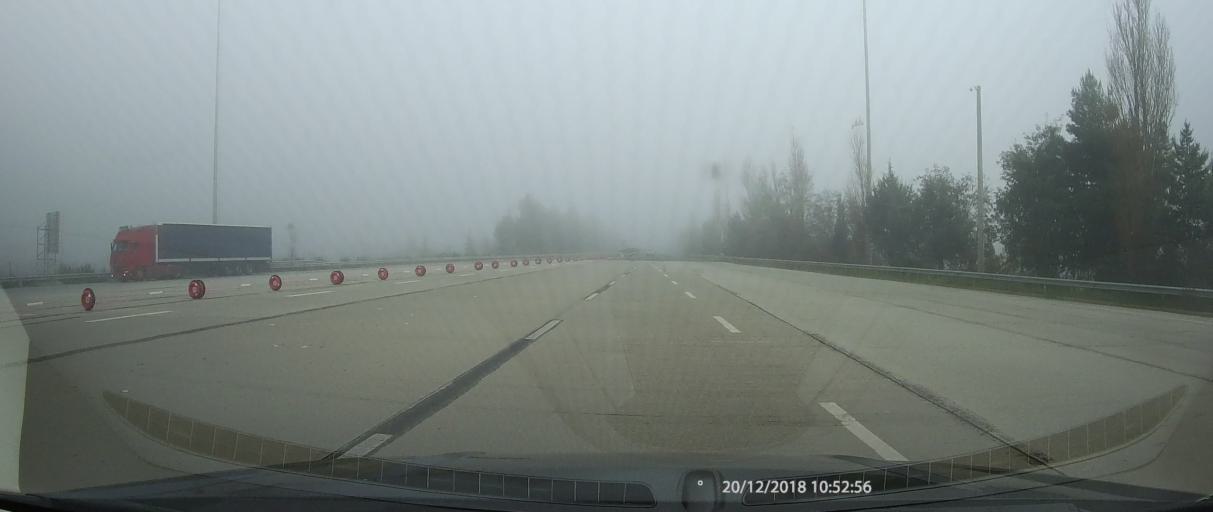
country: GR
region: Peloponnese
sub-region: Nomos Arkadias
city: Tripoli
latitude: 37.6012
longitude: 22.4472
